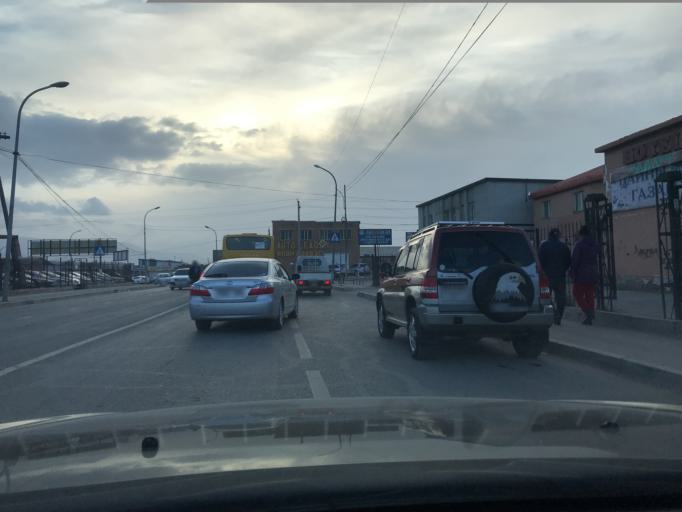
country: MN
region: Ulaanbaatar
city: Ulaanbaatar
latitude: 47.9271
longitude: 106.9993
